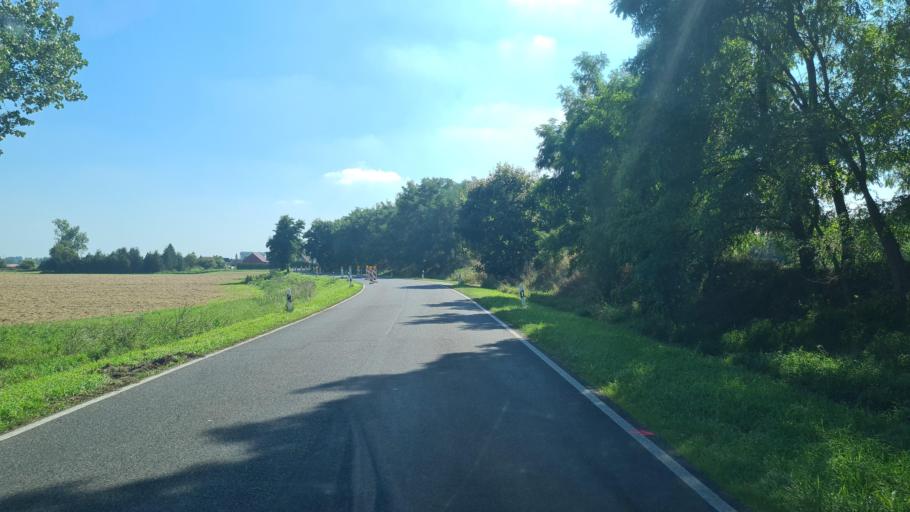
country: DE
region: Brandenburg
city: Friesack
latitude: 52.7179
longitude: 12.6380
